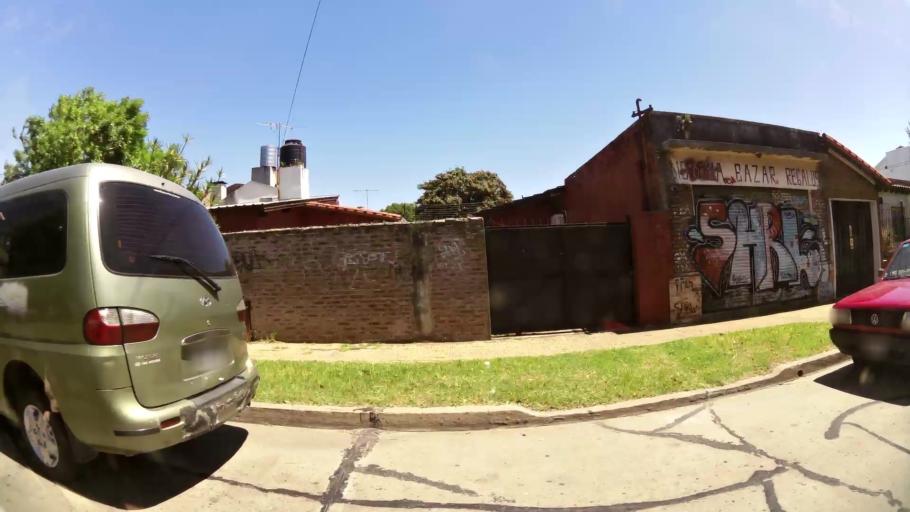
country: AR
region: Buenos Aires
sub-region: Partido de San Isidro
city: San Isidro
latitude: -34.5007
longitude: -58.5756
